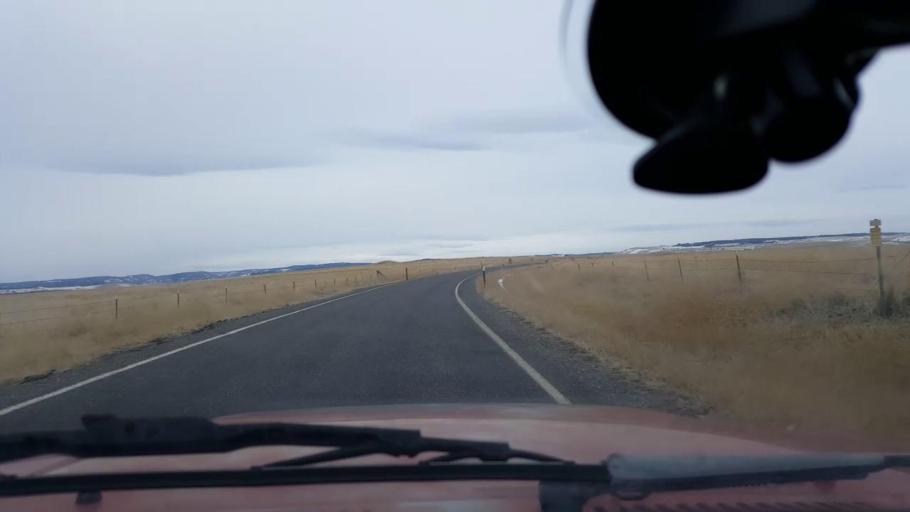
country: US
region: Washington
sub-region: Asotin County
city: Clarkston Heights-Vineland
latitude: 46.3146
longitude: -117.3307
